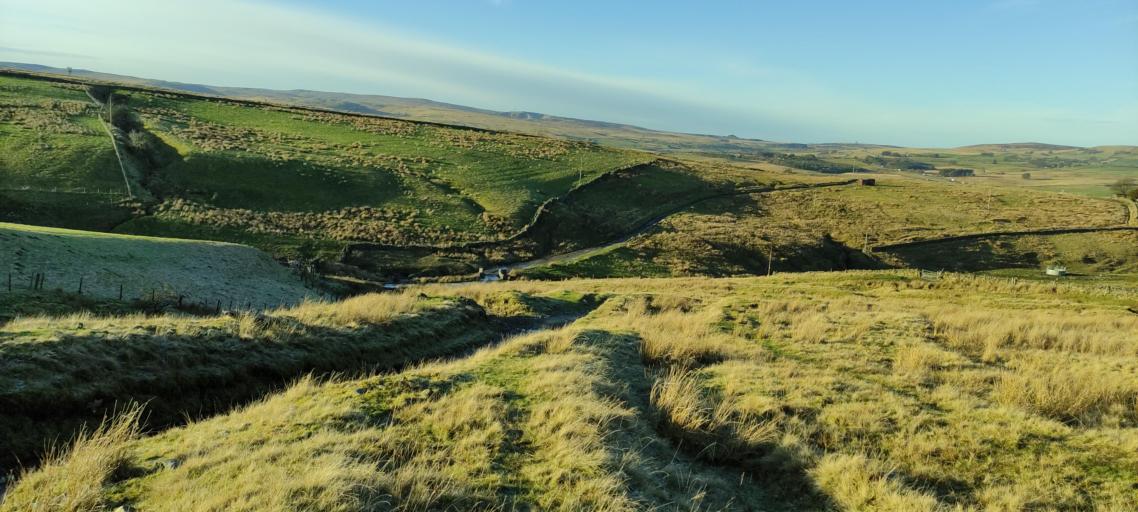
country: GB
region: England
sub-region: Cumbria
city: Sedbergh
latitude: 54.4293
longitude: -2.5825
